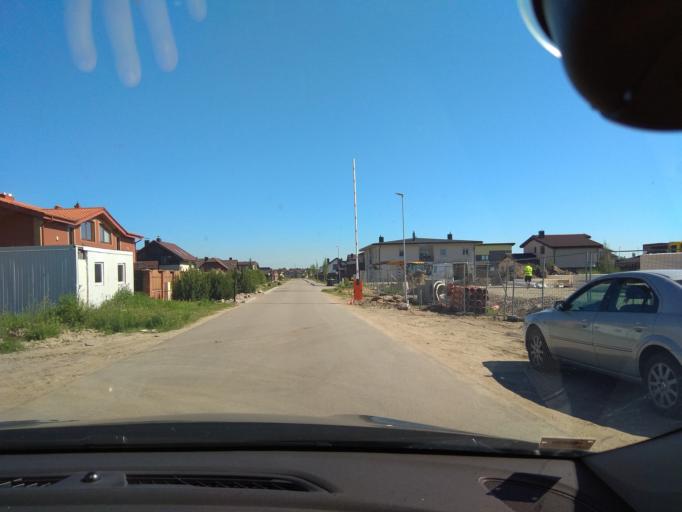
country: LT
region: Klaipedos apskritis
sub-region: Klaipeda
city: Klaipeda
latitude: 55.7526
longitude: 21.1759
